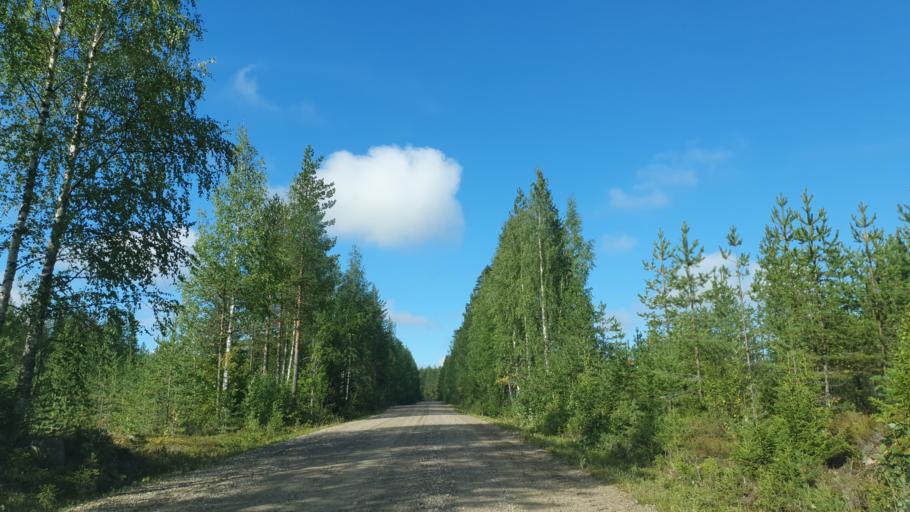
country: FI
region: Kainuu
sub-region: Kehys-Kainuu
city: Kuhmo
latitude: 64.0368
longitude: 29.1515
